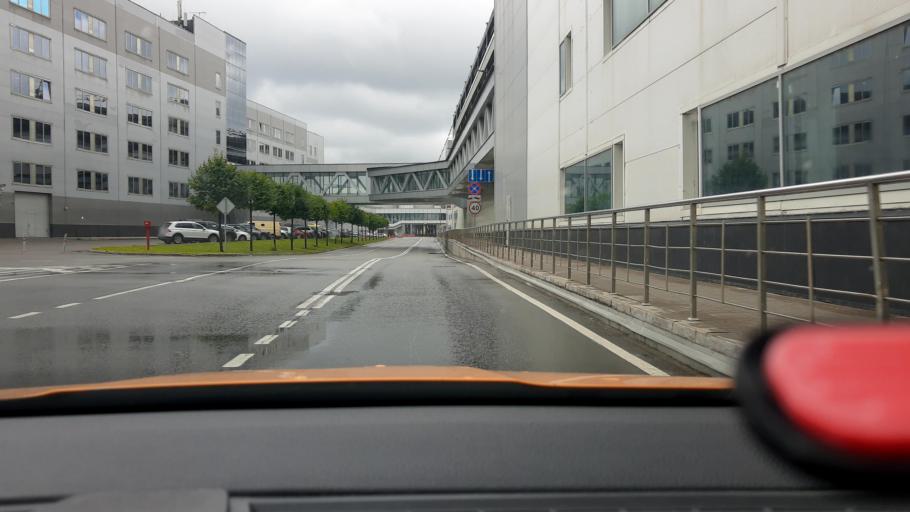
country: RU
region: Moscow
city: Strogino
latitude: 55.8259
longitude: 37.3855
